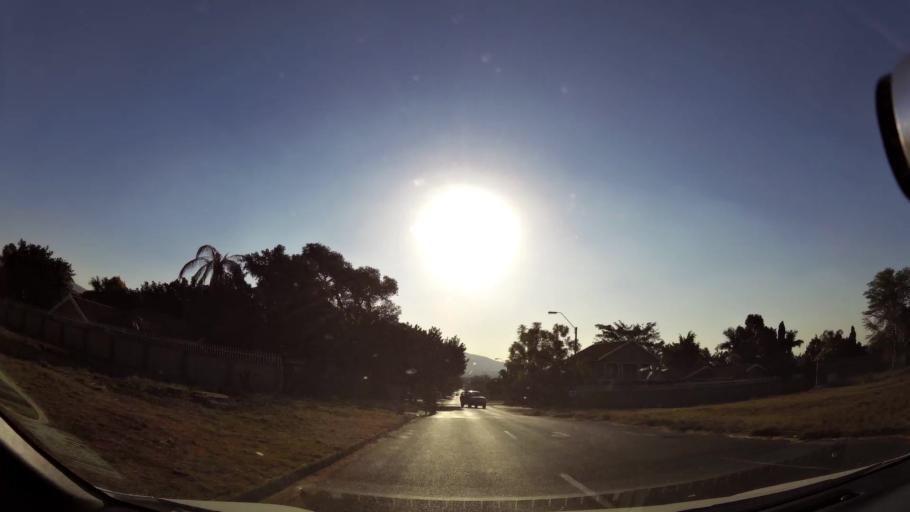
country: ZA
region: North-West
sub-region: Bojanala Platinum District Municipality
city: Rustenburg
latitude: -25.6853
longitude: 27.2397
